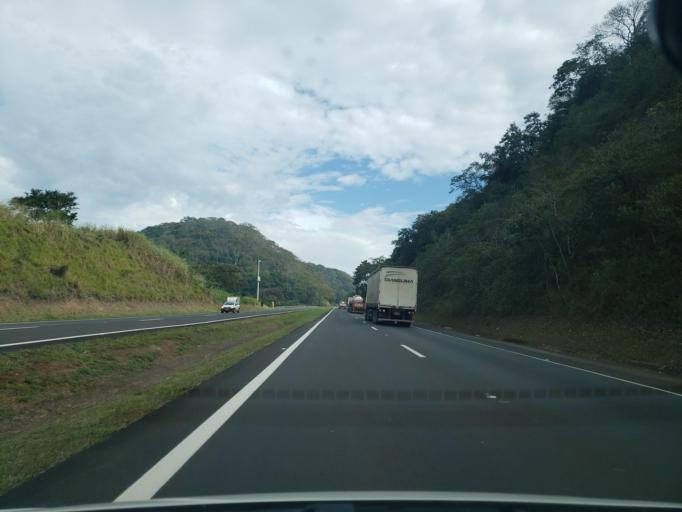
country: BR
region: Sao Paulo
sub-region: Dois Corregos
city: Dois Corregos
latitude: -22.2496
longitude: -48.3396
